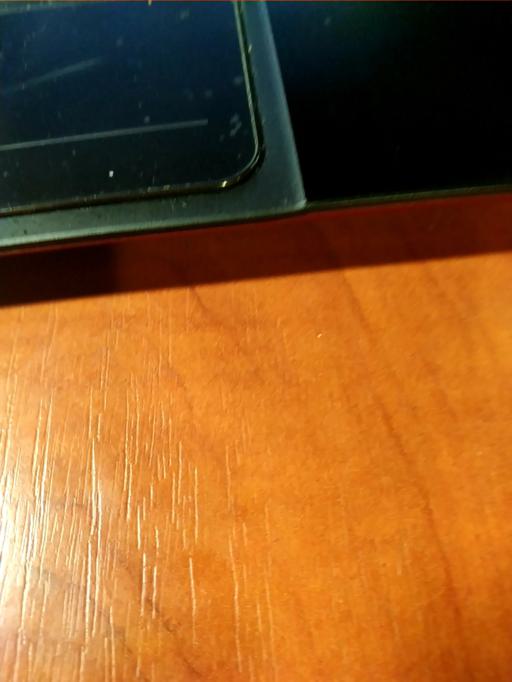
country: RU
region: Tverskaya
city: Zubtsov
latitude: 56.3343
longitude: 34.6729
